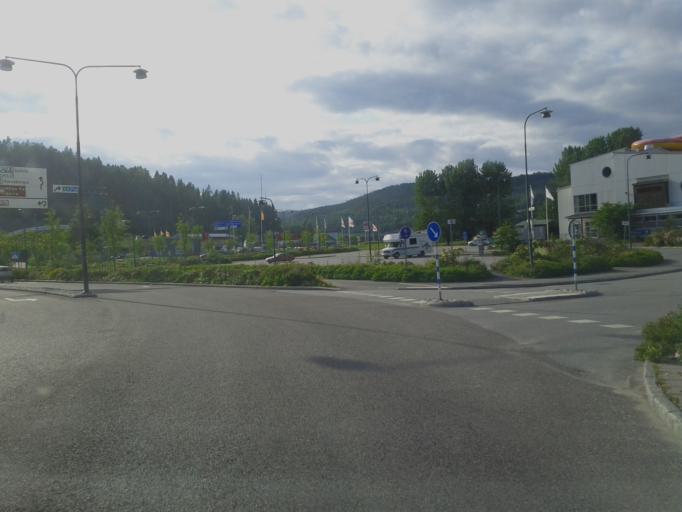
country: SE
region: Vaesternorrland
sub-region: OErnskoeldsviks Kommun
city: Ornskoldsvik
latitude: 63.2893
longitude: 18.7095
